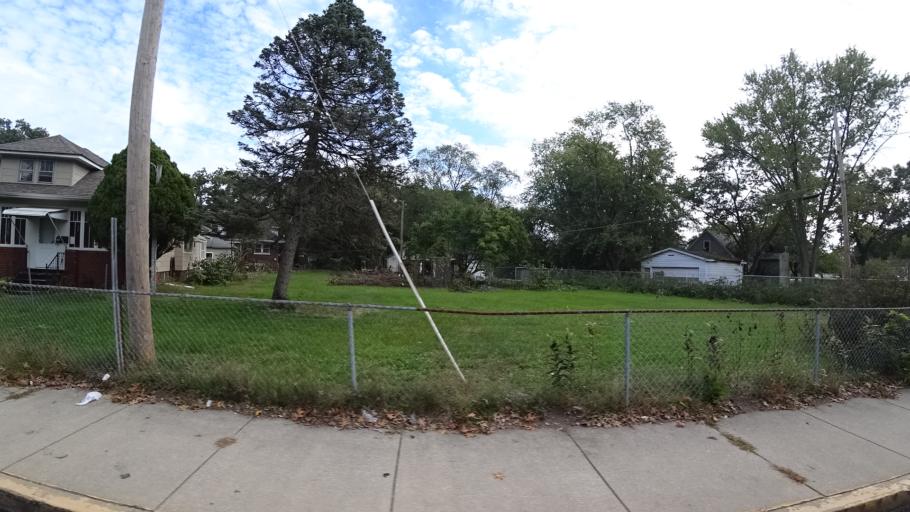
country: US
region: Indiana
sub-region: LaPorte County
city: Michigan City
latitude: 41.7140
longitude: -86.8845
